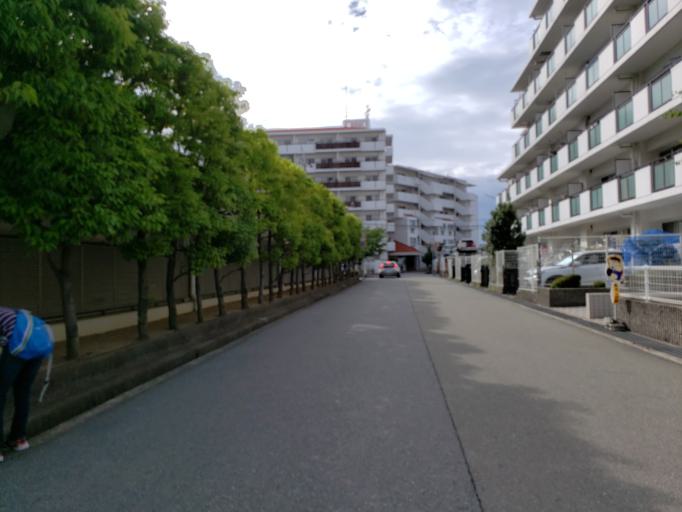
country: JP
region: Hyogo
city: Kakogawacho-honmachi
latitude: 34.7686
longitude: 134.8207
